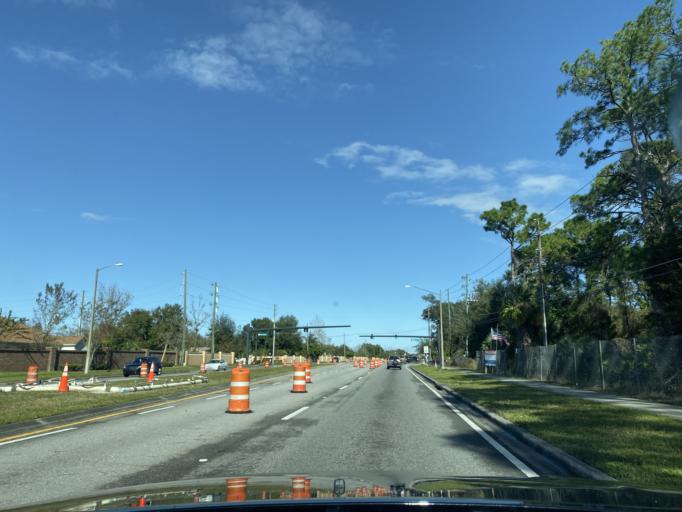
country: US
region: Florida
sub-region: Orange County
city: Alafaya
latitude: 28.5890
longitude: -81.2450
